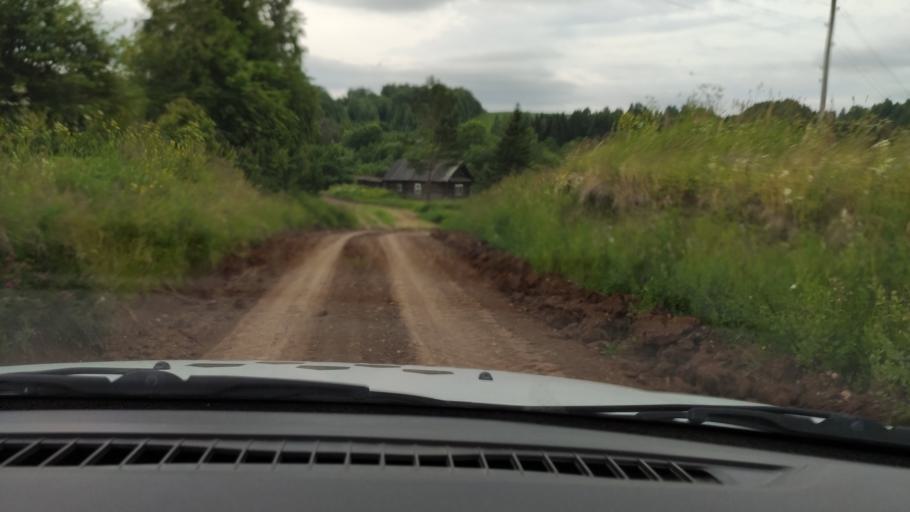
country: RU
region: Perm
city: Orda
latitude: 57.2923
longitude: 56.5939
